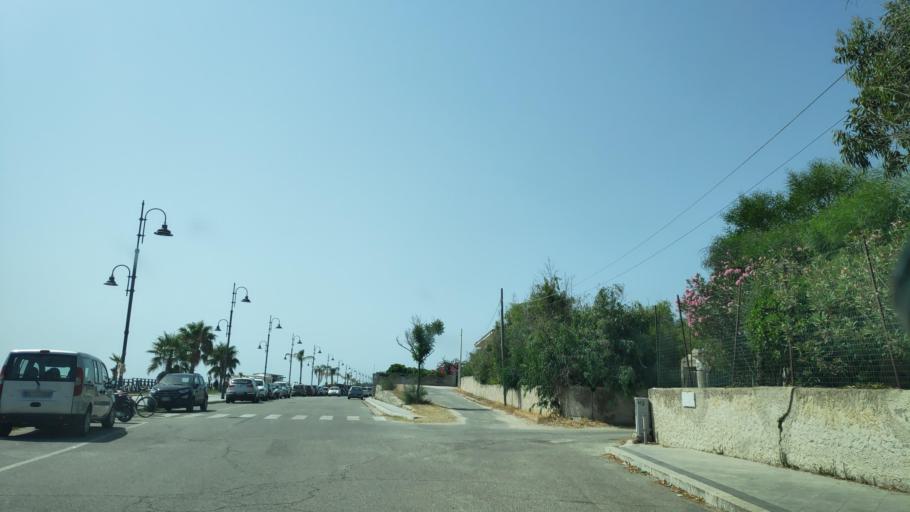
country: IT
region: Calabria
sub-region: Provincia di Catanzaro
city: Guardavalle Marina
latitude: 38.4823
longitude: 16.5799
